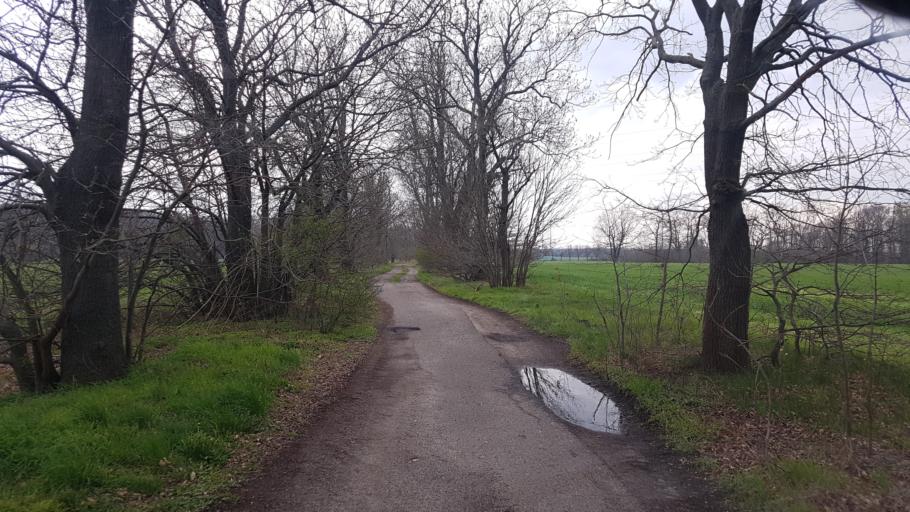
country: DE
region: Brandenburg
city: Bronkow
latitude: 51.6138
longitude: 13.9067
